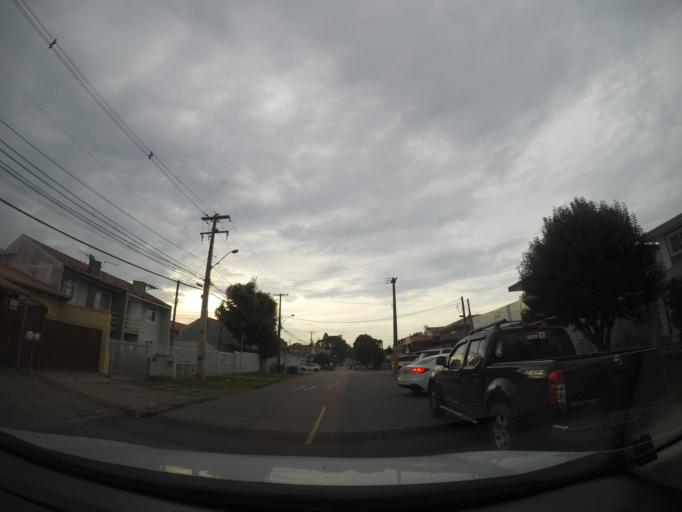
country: BR
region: Parana
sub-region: Sao Jose Dos Pinhais
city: Sao Jose dos Pinhais
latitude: -25.5147
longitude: -49.2394
